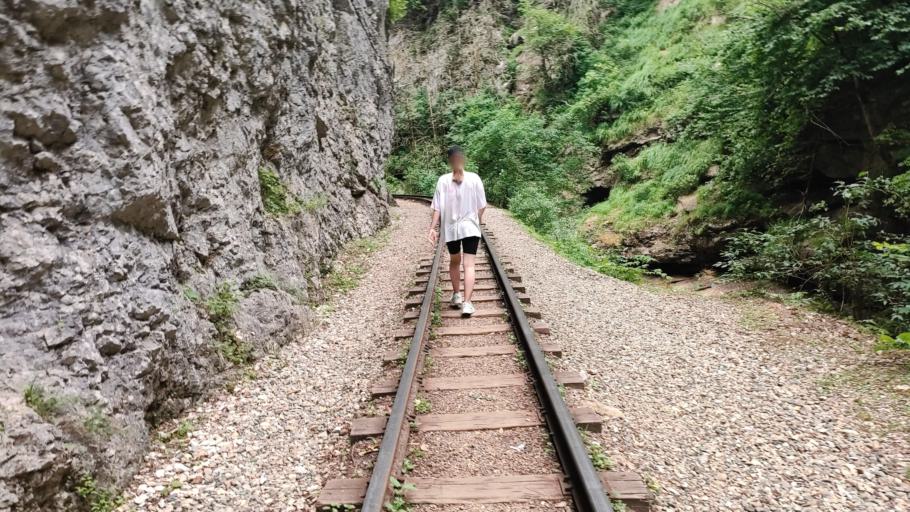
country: RU
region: Krasnodarskiy
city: Neftegorsk
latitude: 44.2166
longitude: 39.9148
